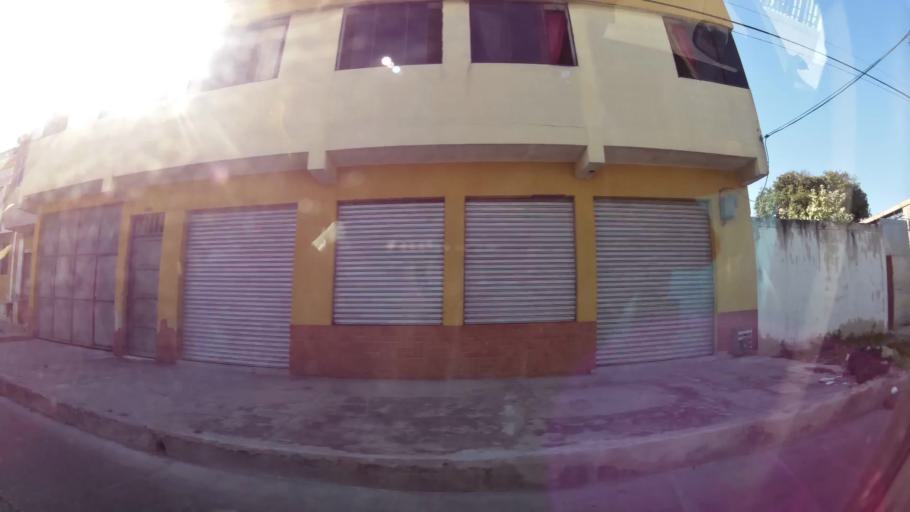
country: CO
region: Atlantico
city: Barranquilla
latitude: 10.9741
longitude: -74.7811
